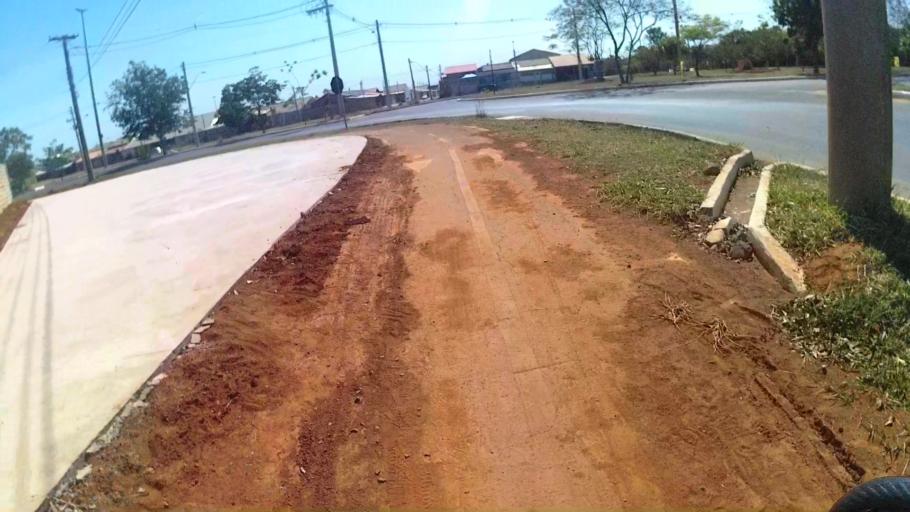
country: BR
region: Federal District
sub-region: Brasilia
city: Brasilia
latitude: -15.9052
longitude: -48.0424
